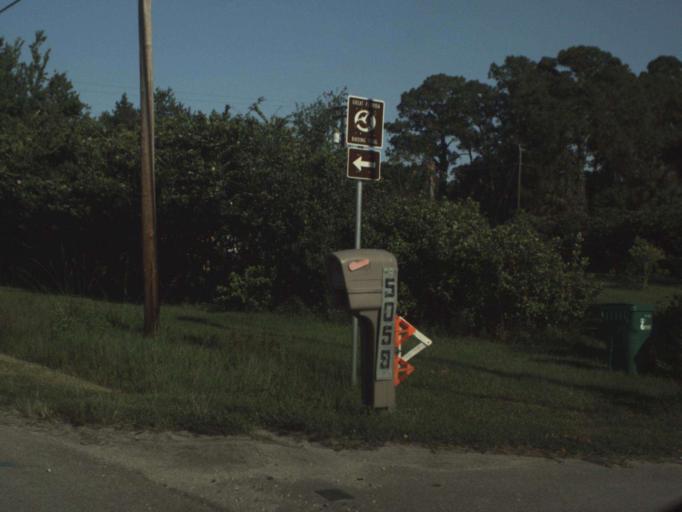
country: US
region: Florida
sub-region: Brevard County
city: Mims
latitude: 28.6659
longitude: -80.8897
